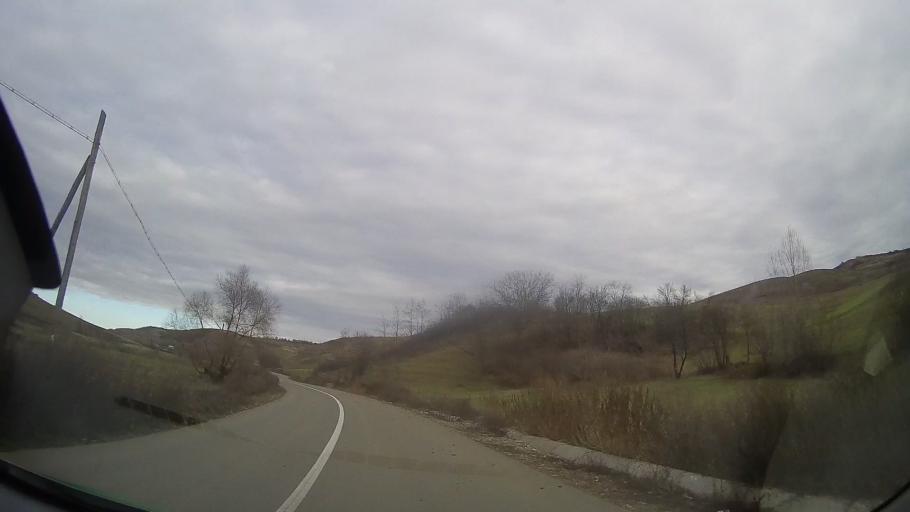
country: RO
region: Bistrita-Nasaud
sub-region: Comuna Silvasu de Campie
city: Silvasu de Campie
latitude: 46.8235
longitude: 24.3031
